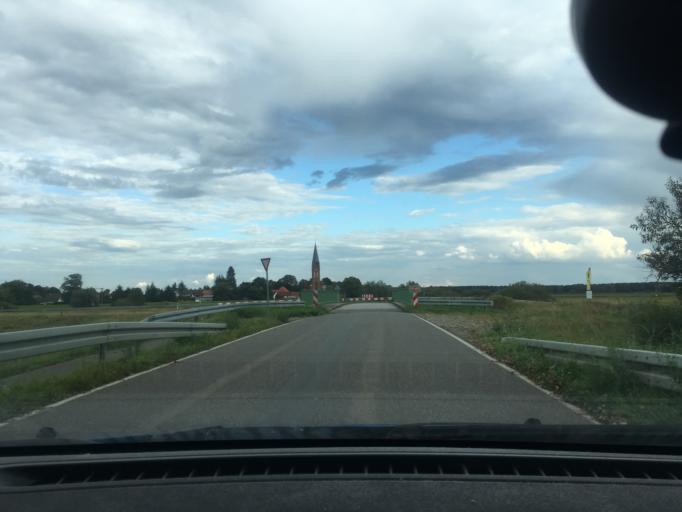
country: DE
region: Mecklenburg-Vorpommern
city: Boizenburg
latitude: 53.3550
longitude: 10.8223
